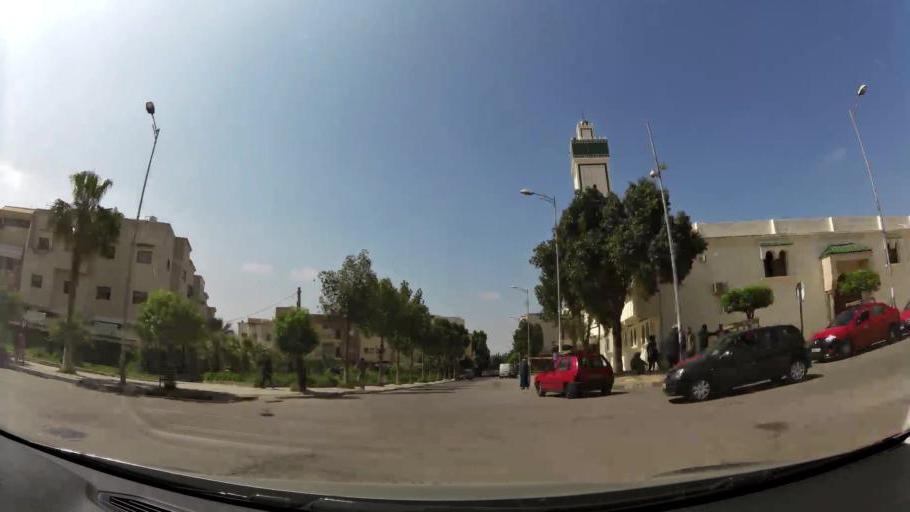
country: MA
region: Fes-Boulemane
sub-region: Fes
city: Fes
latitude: 34.0550
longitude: -5.0326
